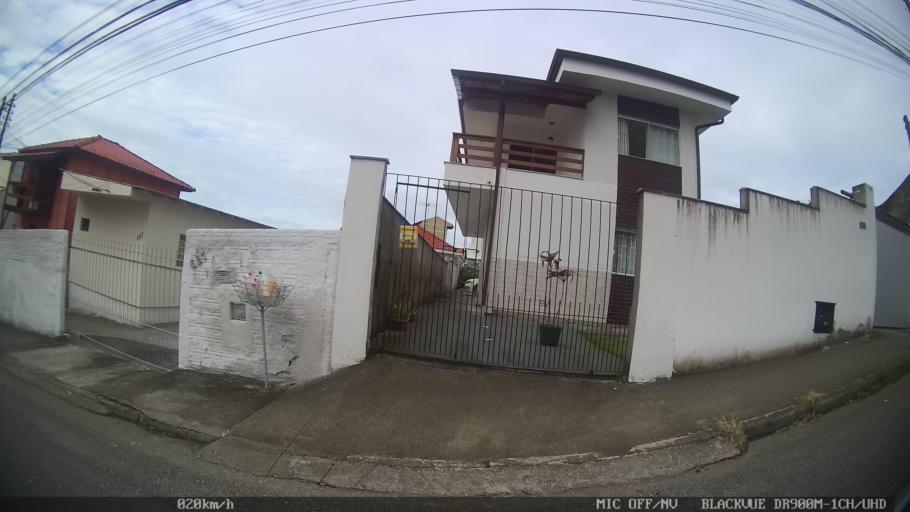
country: BR
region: Santa Catarina
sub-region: Sao Jose
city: Campinas
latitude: -27.5781
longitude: -48.6044
